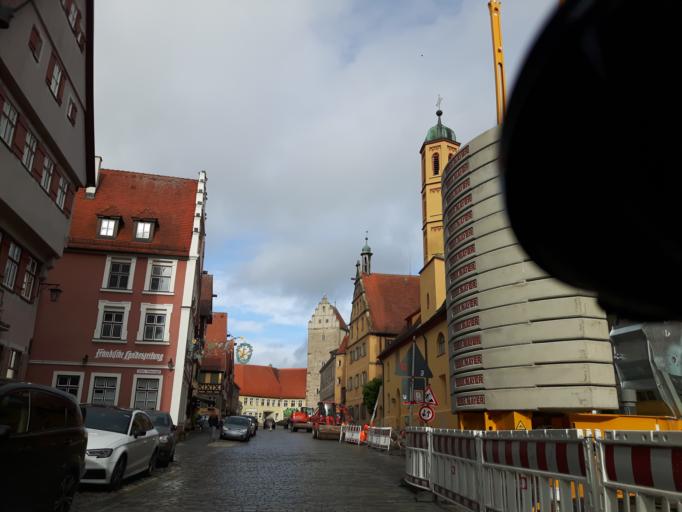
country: DE
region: Bavaria
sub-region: Regierungsbezirk Mittelfranken
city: Dinkelsbuhl
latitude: 49.0704
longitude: 10.3187
